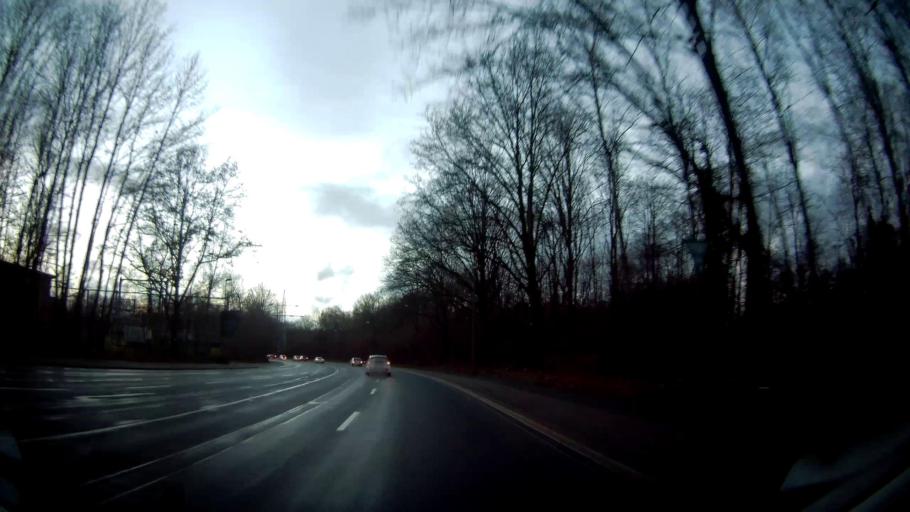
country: DE
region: North Rhine-Westphalia
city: Castrop-Rauxel
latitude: 51.4914
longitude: 7.3018
